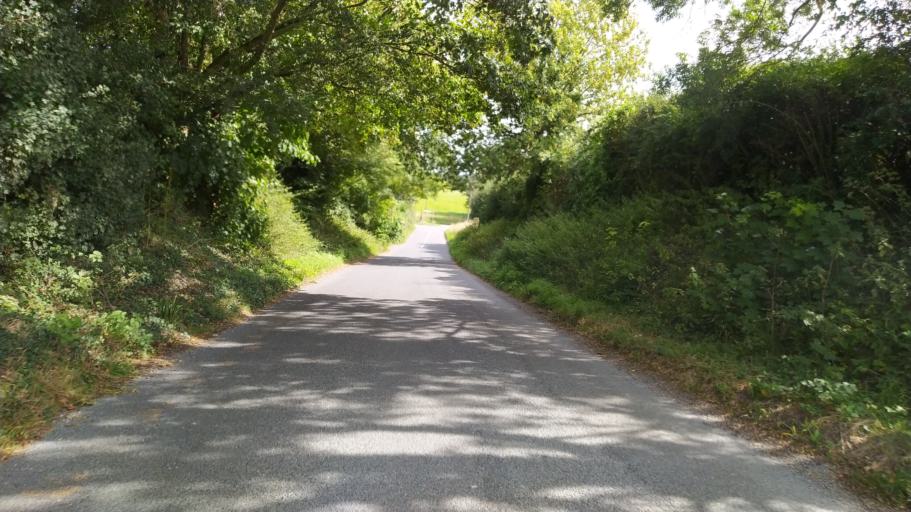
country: GB
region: England
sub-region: Dorset
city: Blandford Forum
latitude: 50.8247
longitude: -2.1120
